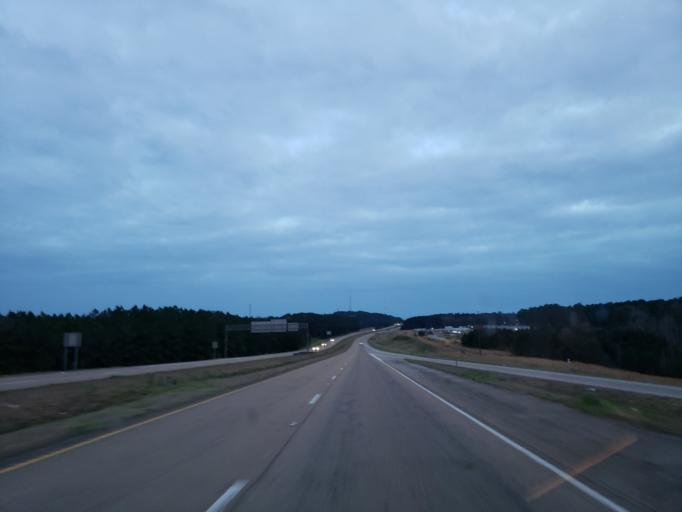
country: US
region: Mississippi
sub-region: Lauderdale County
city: Marion
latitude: 32.3802
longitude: -88.6363
